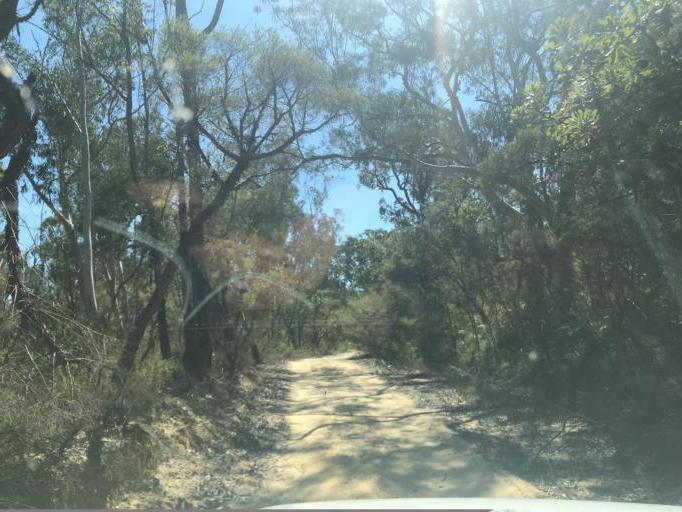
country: AU
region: New South Wales
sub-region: Wyong Shire
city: Little Jilliby
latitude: -33.1501
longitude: 151.1005
